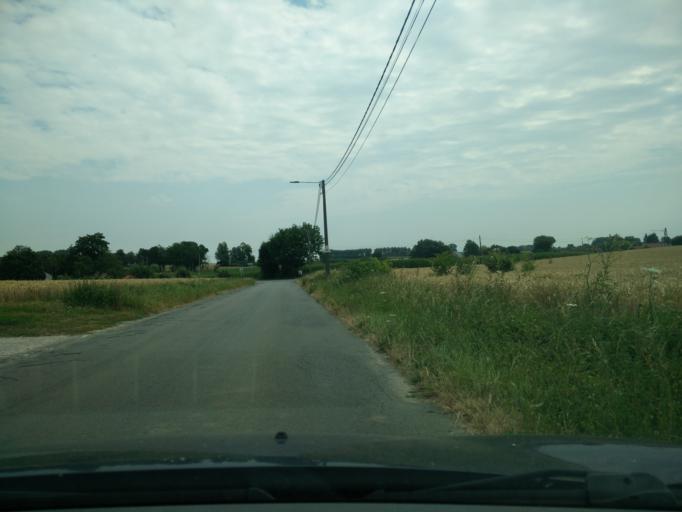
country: BE
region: Wallonia
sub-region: Province du Hainaut
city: Roeulx
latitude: 50.5520
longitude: 4.1131
